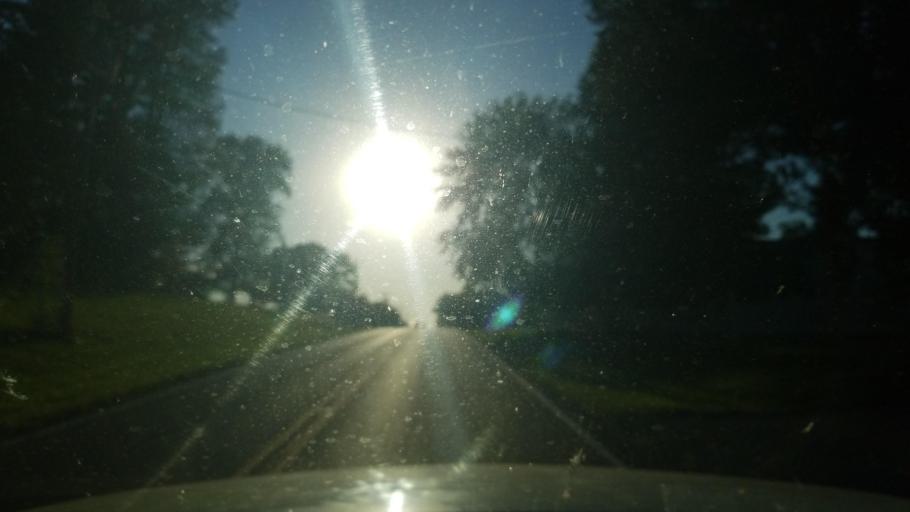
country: US
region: Illinois
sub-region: Saline County
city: Harrisburg
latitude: 37.6364
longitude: -88.4888
